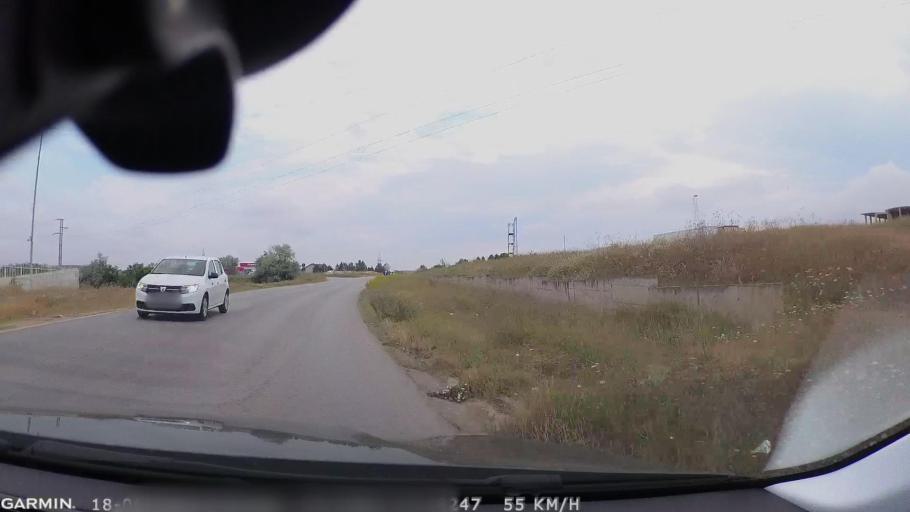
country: MK
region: Stip
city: Shtip
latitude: 41.7732
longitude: 22.1825
